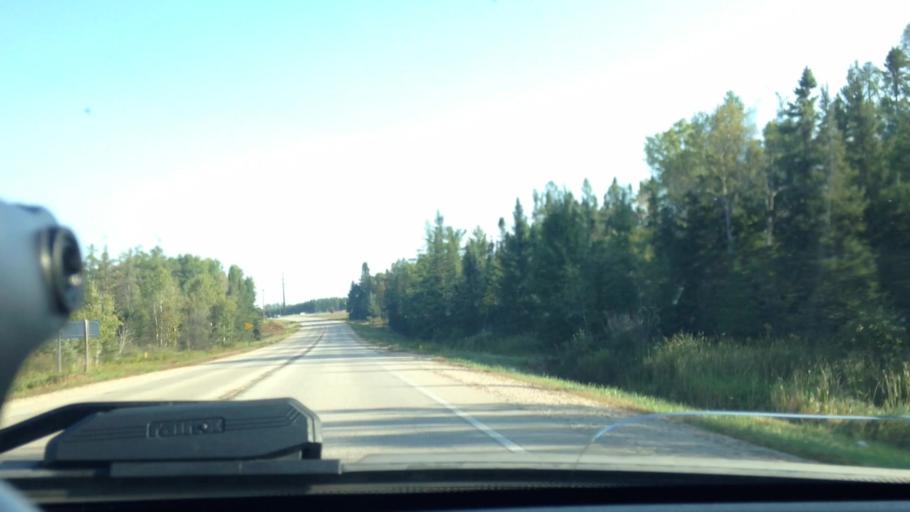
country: US
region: Wisconsin
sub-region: Marinette County
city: Niagara
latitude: 45.4339
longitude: -87.9774
